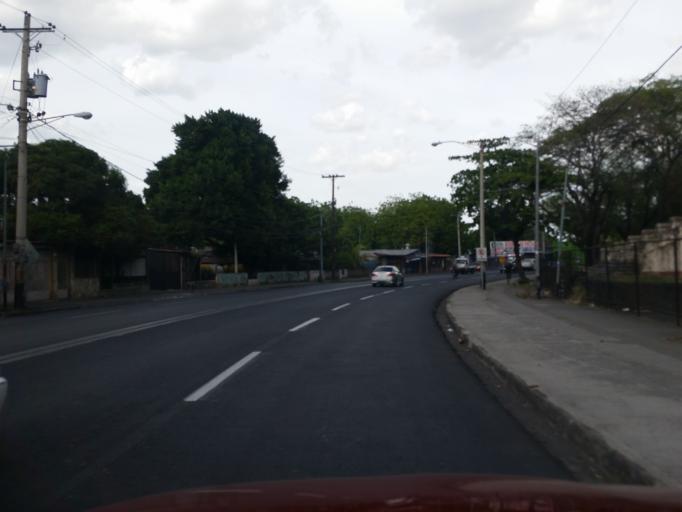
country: NI
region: Managua
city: Managua
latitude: 12.1456
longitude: -86.2719
